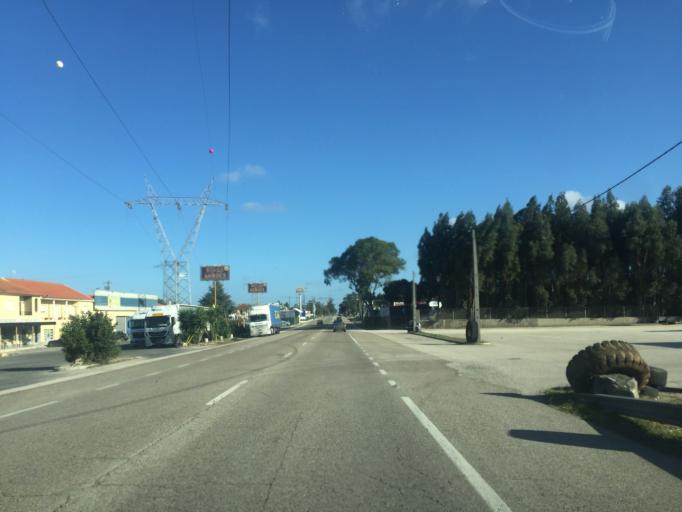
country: PT
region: Leiria
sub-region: Alcobaca
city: Turquel
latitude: 39.4615
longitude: -8.9450
